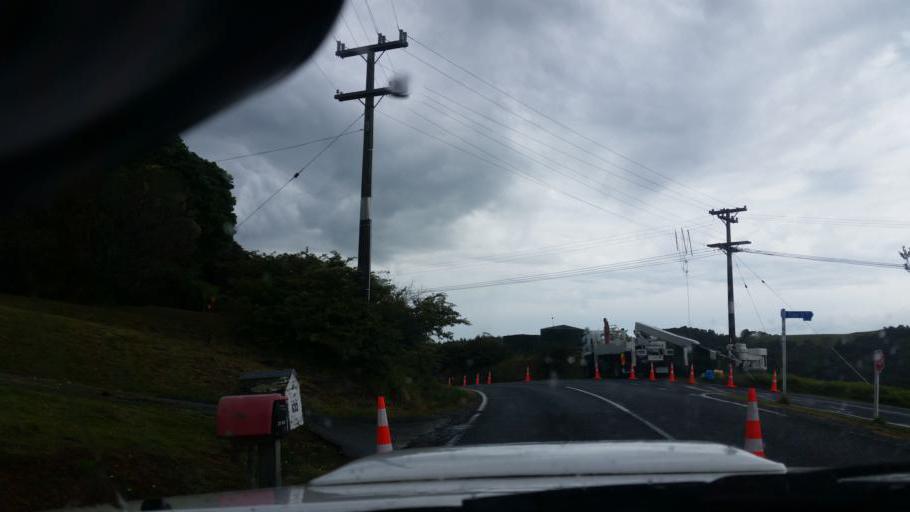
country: NZ
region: Auckland
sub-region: Auckland
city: Wellsford
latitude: -36.1550
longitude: 174.2263
